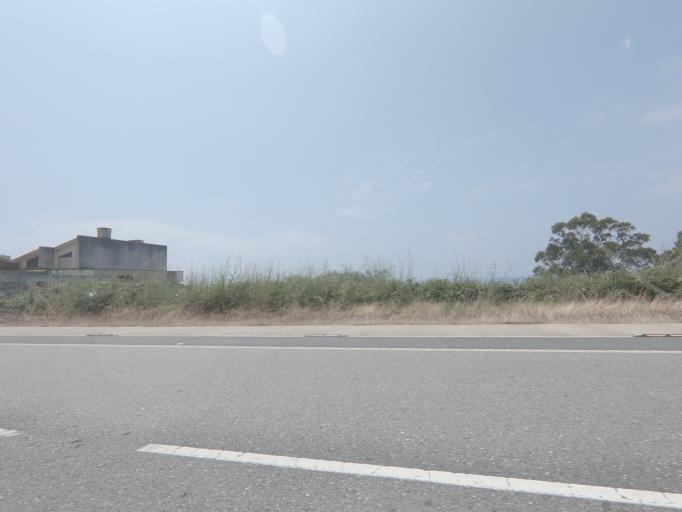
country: ES
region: Galicia
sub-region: Provincia de Pontevedra
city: A Guarda
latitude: 41.9170
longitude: -8.8796
